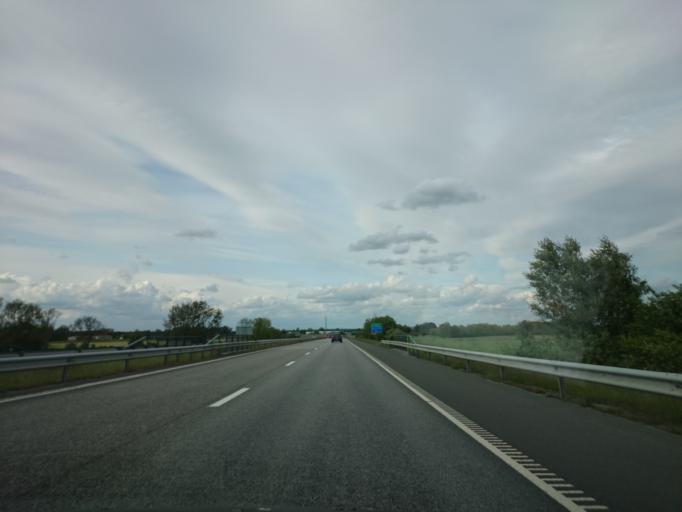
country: SE
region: Skane
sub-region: Kristianstads Kommun
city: Norra Asum
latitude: 55.9918
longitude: 14.0940
